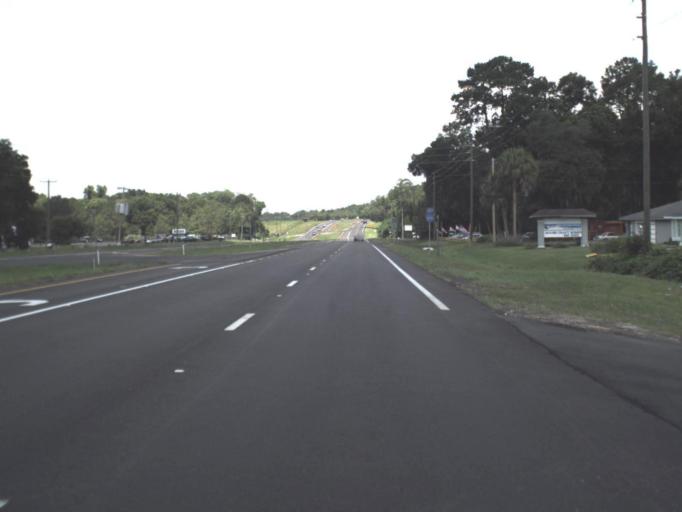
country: US
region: Florida
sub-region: Alachua County
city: Alachua
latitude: 29.7695
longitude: -82.4248
